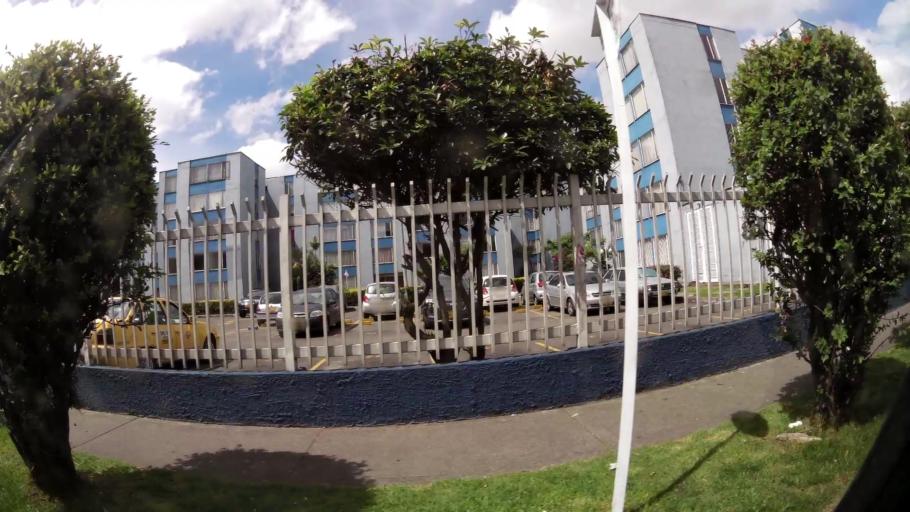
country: CO
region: Bogota D.C.
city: Bogota
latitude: 4.6962
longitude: -74.1077
